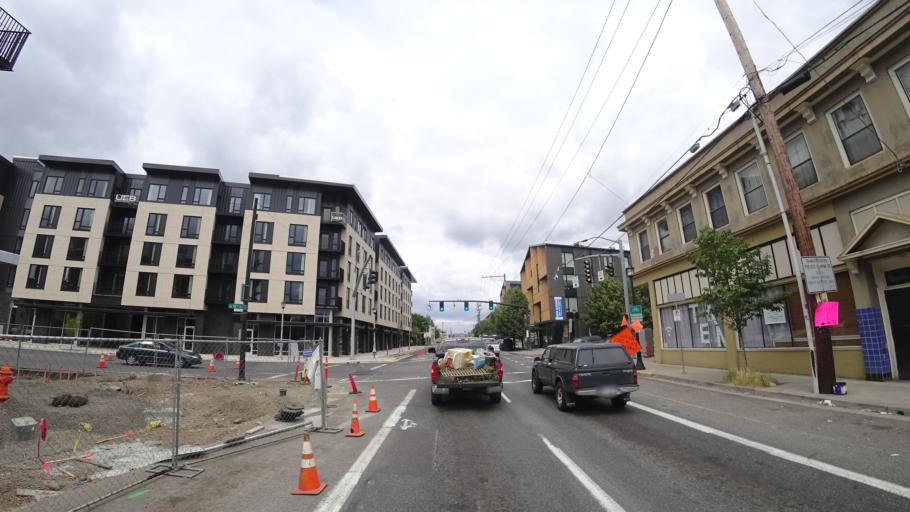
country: US
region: Oregon
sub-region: Multnomah County
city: Lents
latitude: 45.4797
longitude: -122.5683
